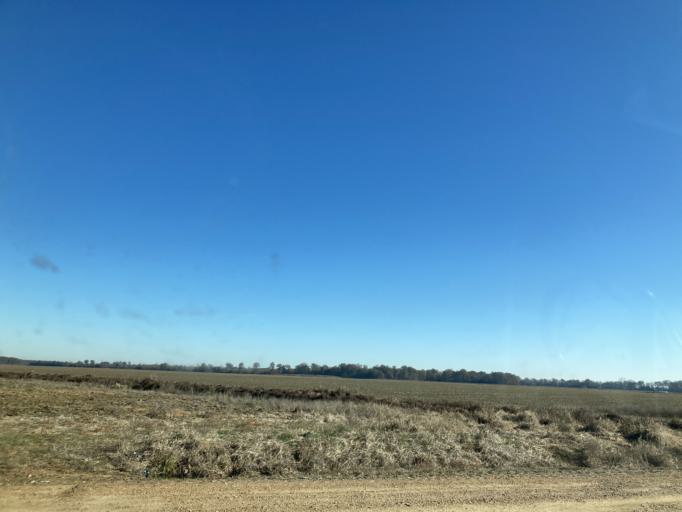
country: US
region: Mississippi
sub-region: Sharkey County
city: Rolling Fork
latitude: 32.9011
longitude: -90.6640
